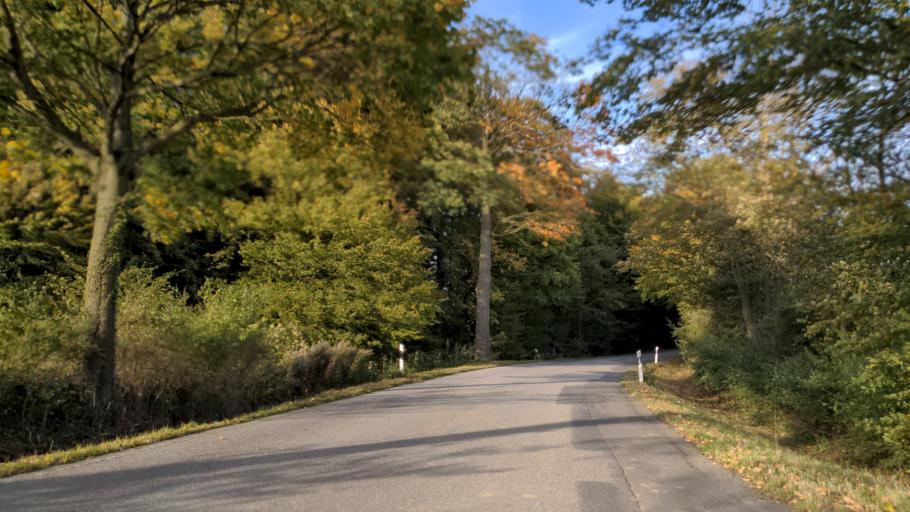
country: DE
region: Schleswig-Holstein
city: Ahrensbok
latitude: 53.9827
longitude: 10.5645
